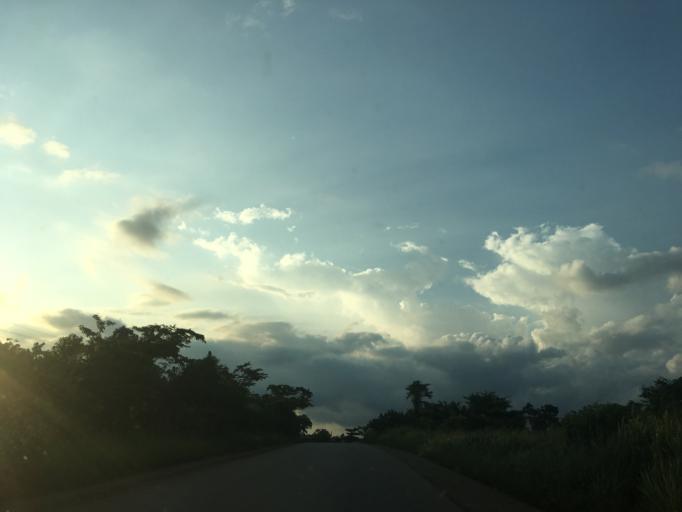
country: GH
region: Western
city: Bibiani
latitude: 6.6643
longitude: -2.4289
